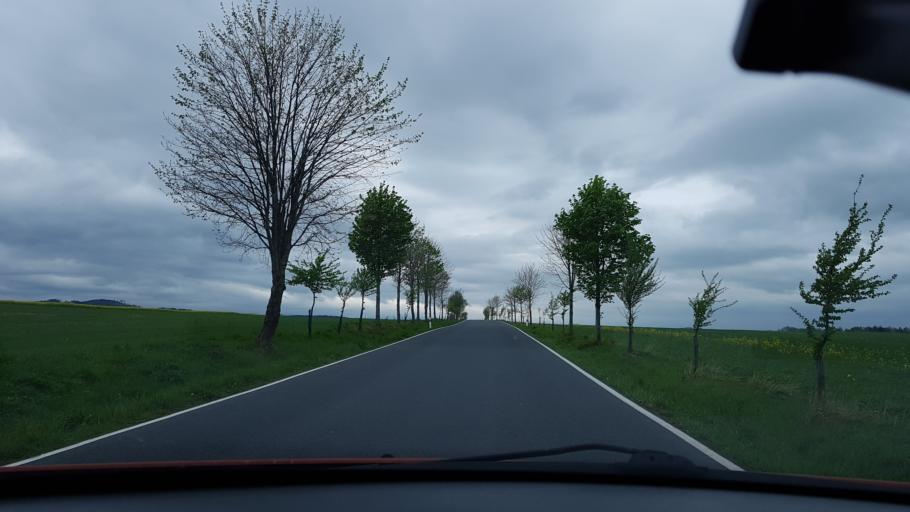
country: CZ
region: Olomoucky
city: Mikulovice
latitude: 50.3084
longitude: 17.3102
